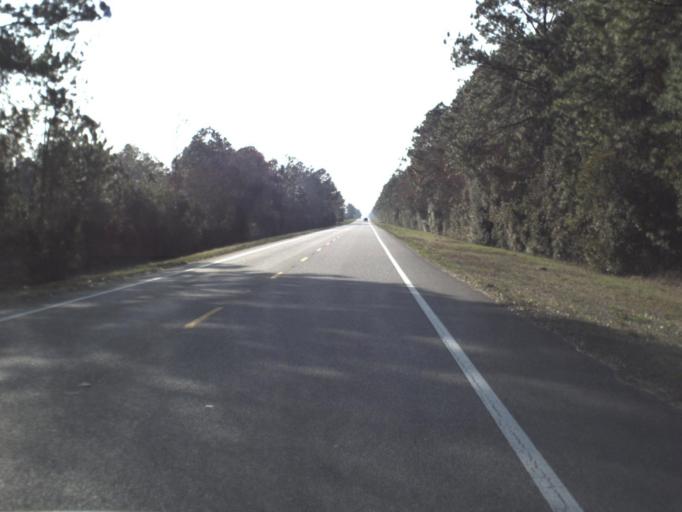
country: US
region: Florida
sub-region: Bay County
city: Lynn Haven
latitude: 30.4395
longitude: -85.7544
